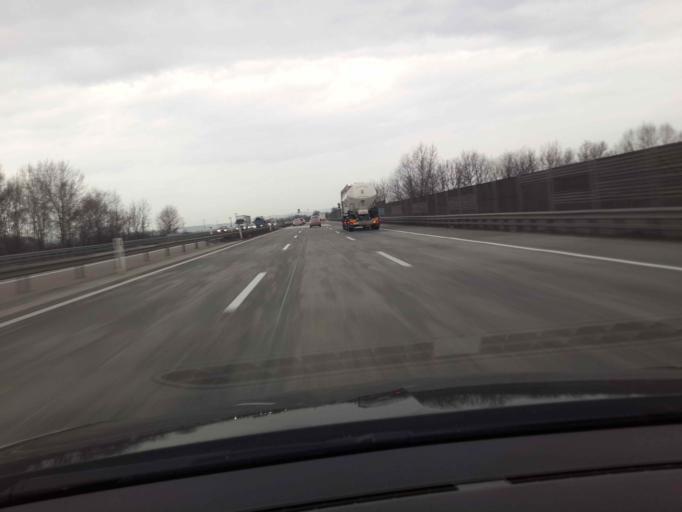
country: AT
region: Lower Austria
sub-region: Politischer Bezirk Sankt Polten
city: Gerersdorf
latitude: 48.1774
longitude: 15.5769
